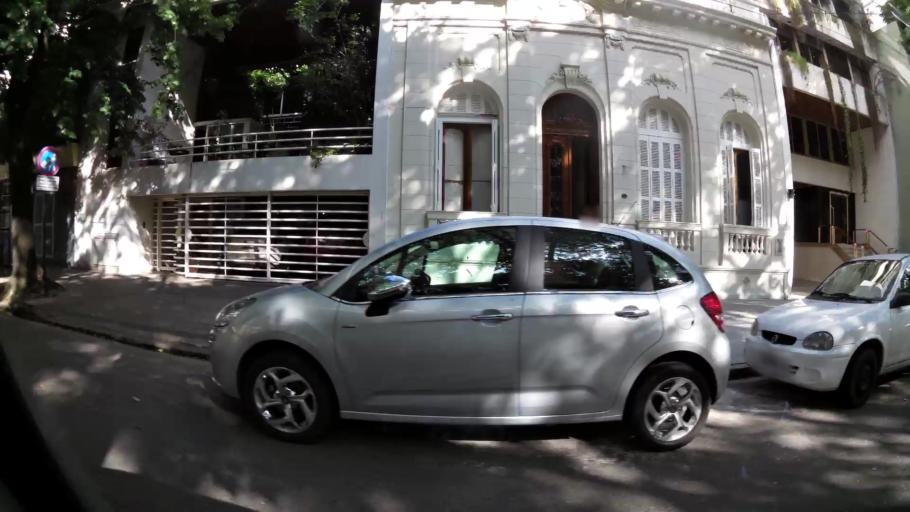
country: AR
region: Buenos Aires
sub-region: Partido de La Plata
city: La Plata
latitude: -34.9146
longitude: -57.9459
